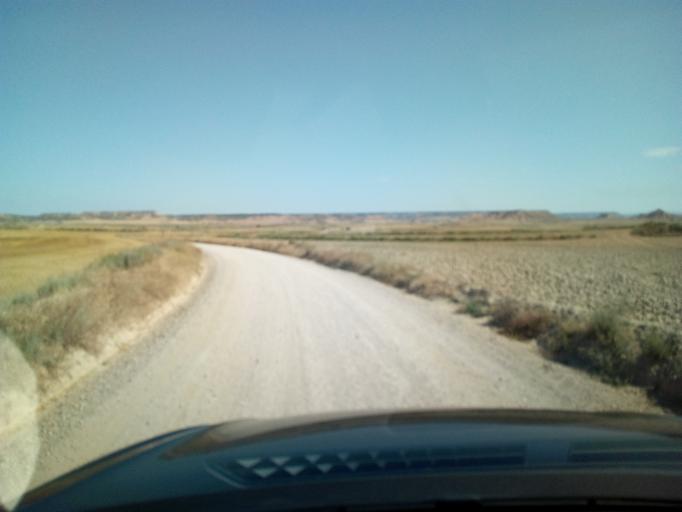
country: ES
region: Navarre
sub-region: Provincia de Navarra
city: Arguedas
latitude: 42.1804
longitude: -1.5215
